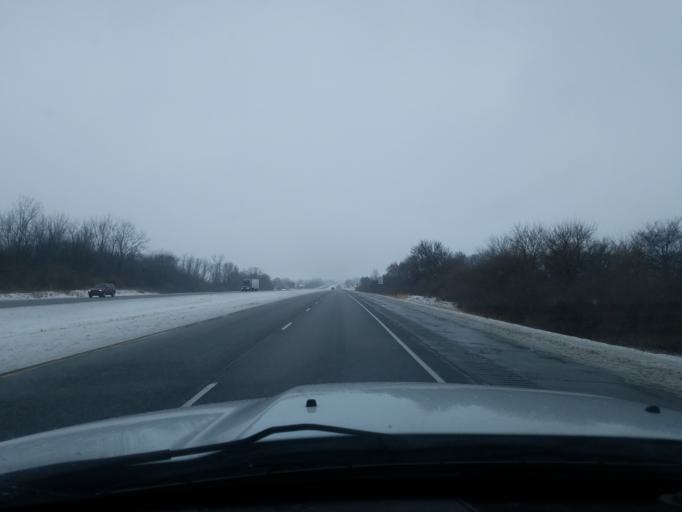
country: US
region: Indiana
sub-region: Fulton County
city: Rochester
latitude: 40.9397
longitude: -86.1683
